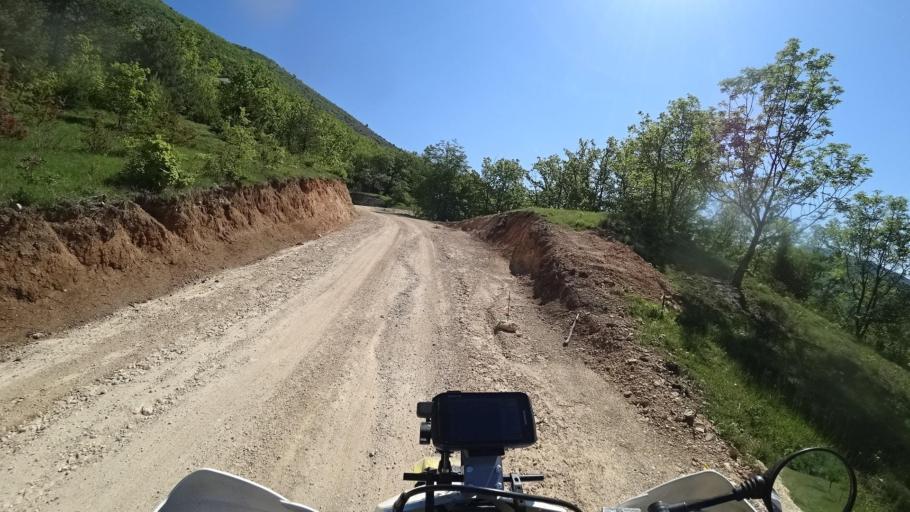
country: BA
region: Federation of Bosnia and Herzegovina
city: Rumboci
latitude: 43.8384
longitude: 17.5288
